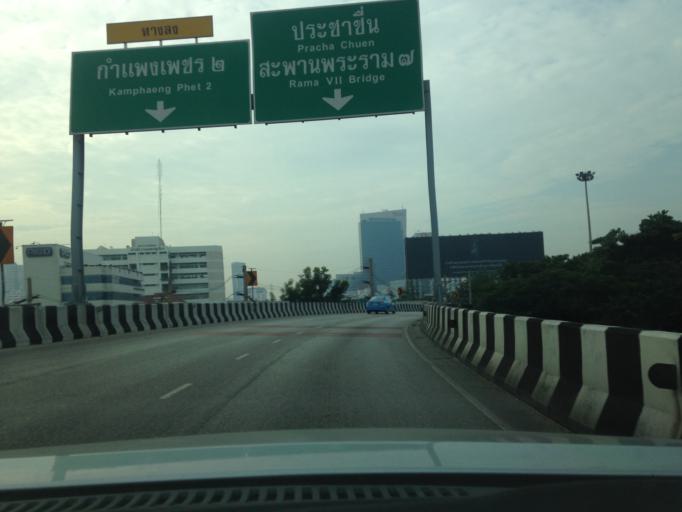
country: TH
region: Bangkok
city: Chatuchak
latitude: 13.8309
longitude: 100.5591
